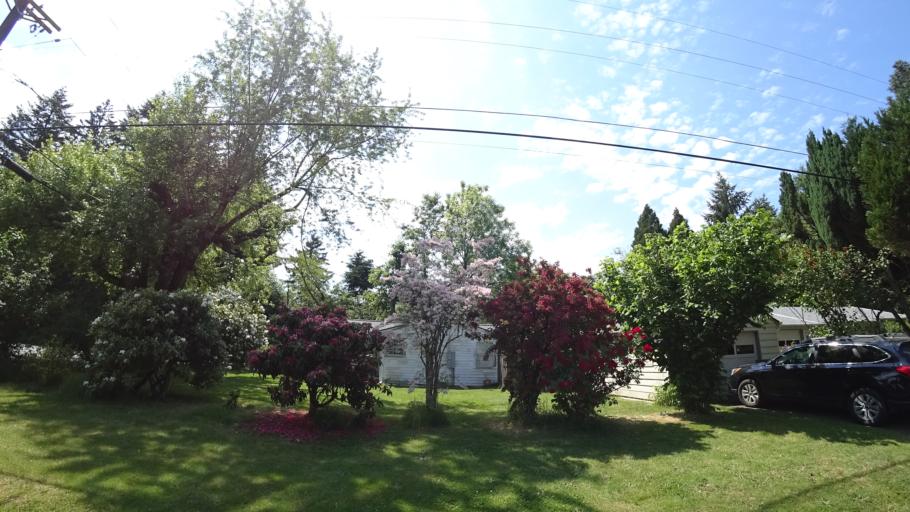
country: US
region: Oregon
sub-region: Washington County
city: Metzger
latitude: 45.4549
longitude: -122.7314
